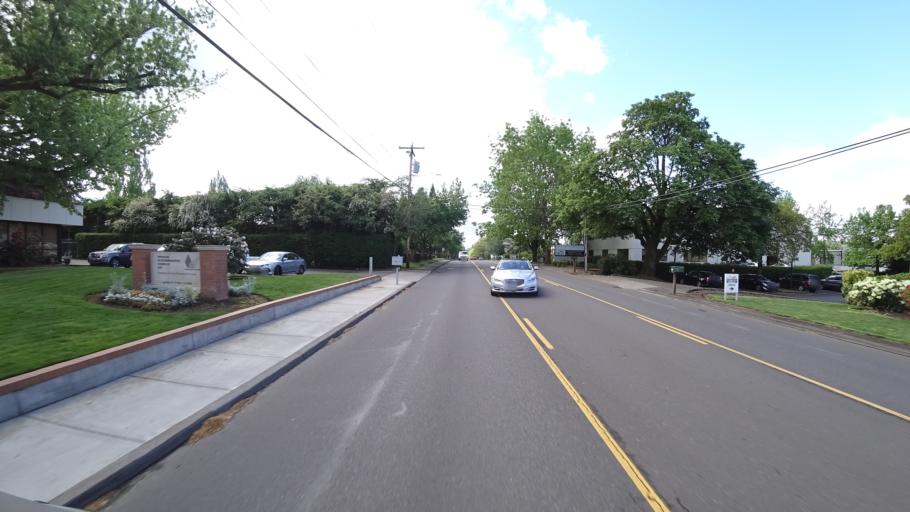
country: US
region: Oregon
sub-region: Washington County
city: Durham
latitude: 45.4129
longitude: -122.7491
